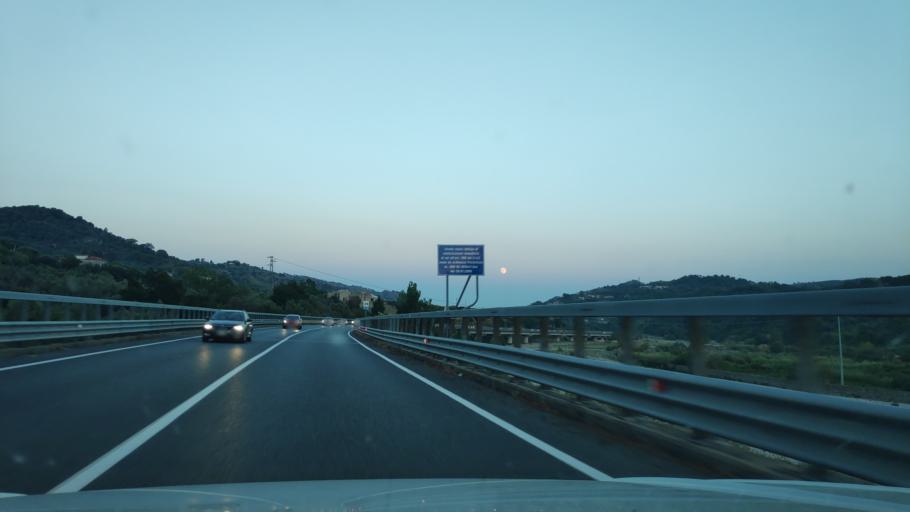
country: IT
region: Calabria
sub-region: Provincia di Reggio Calabria
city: Mammola
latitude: 38.3507
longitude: 16.2512
